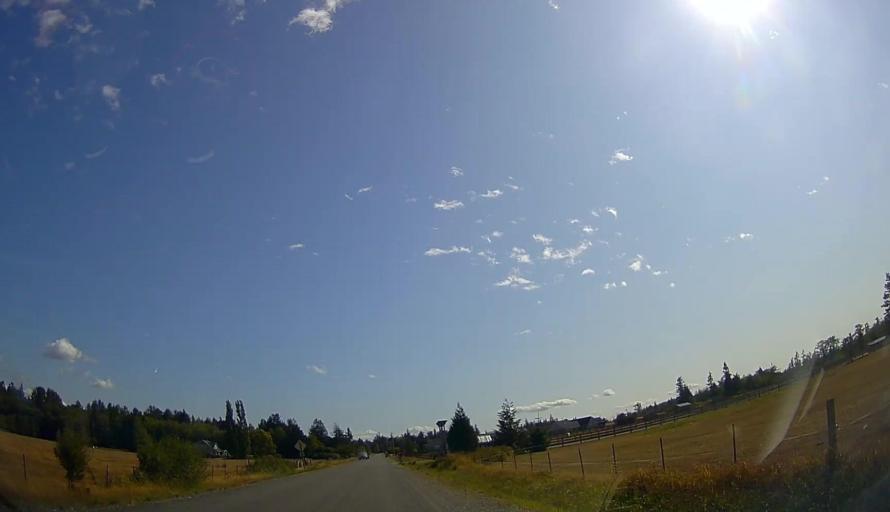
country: US
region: Washington
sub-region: Skagit County
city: Burlington
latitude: 48.4999
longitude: -122.4612
